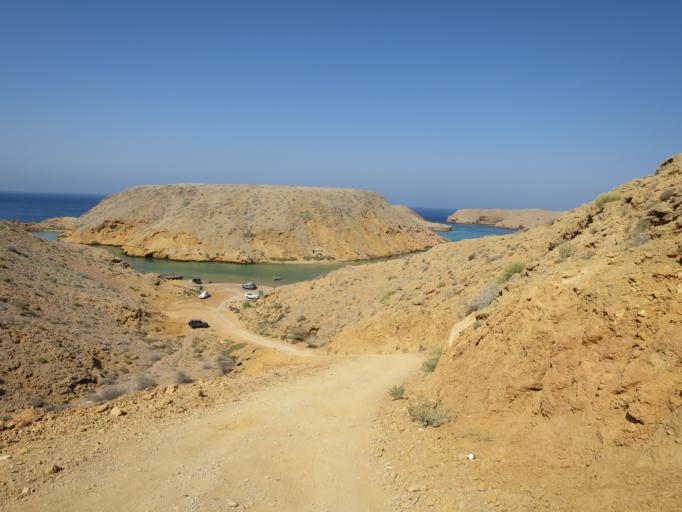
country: OM
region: Muhafazat Masqat
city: Muscat
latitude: 23.5151
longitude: 58.7422
